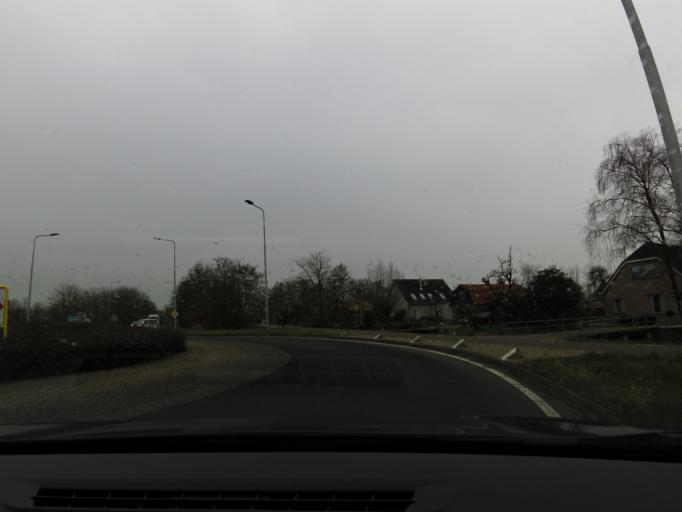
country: NL
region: South Holland
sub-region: Gemeente Nieuwkoop
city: Nieuwkoop
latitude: 52.1589
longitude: 4.7805
